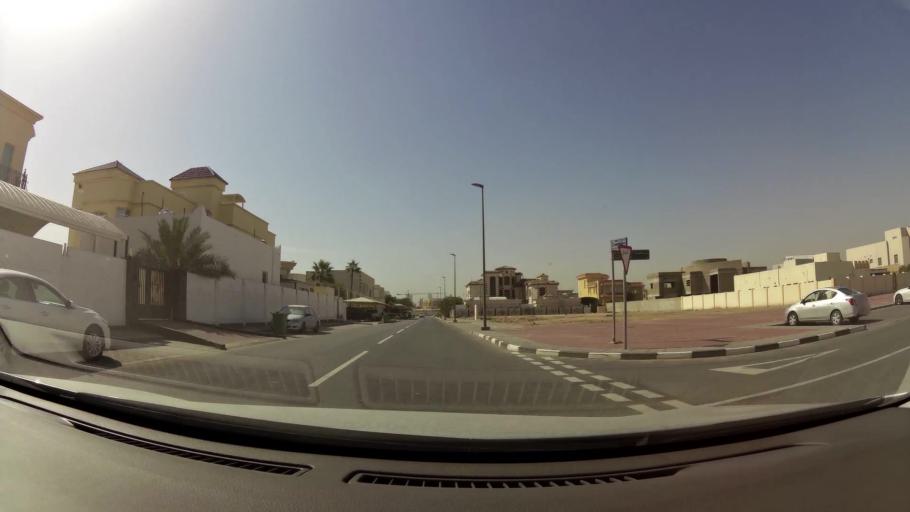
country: QA
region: Baladiyat ad Dawhah
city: Doha
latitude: 25.3596
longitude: 51.5191
